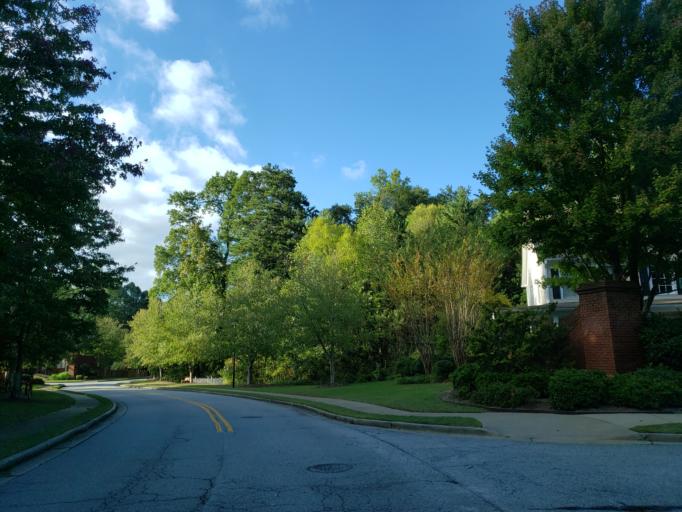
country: US
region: Georgia
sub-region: Cobb County
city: Marietta
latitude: 33.9850
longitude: -84.5009
